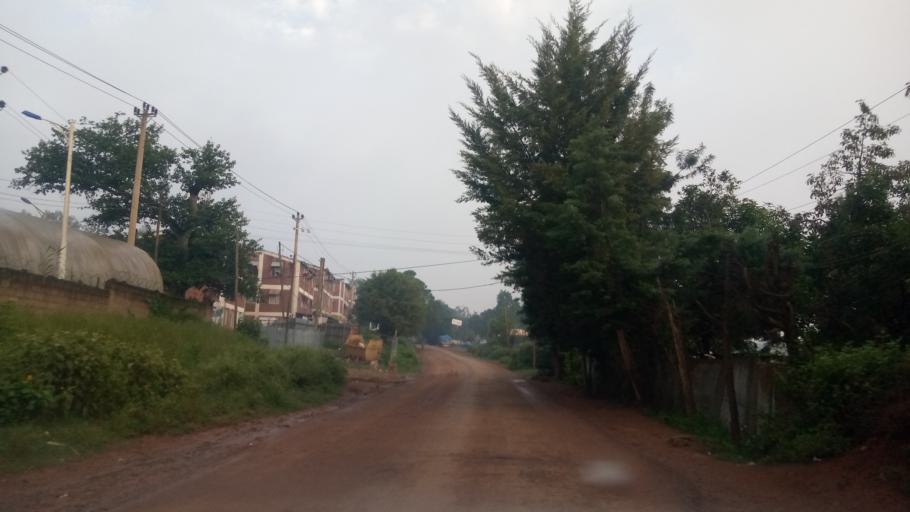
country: ET
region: Oromiya
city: Jima
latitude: 7.6871
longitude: 36.8304
